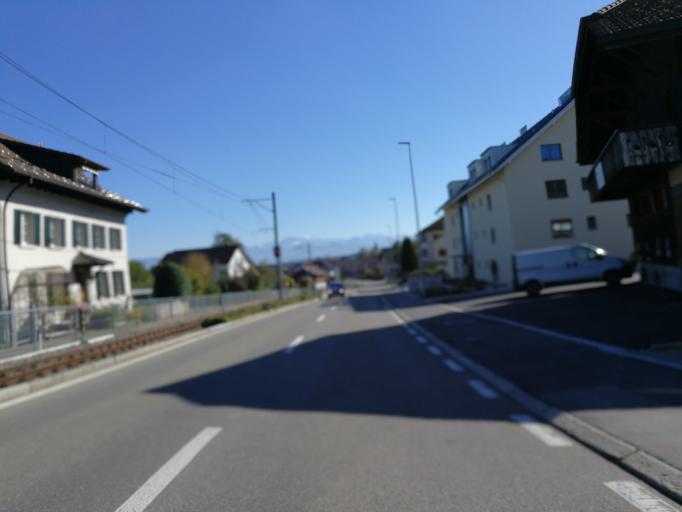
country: CH
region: Zurich
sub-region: Bezirk Uster
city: Hinteregg
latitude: 47.3081
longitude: 8.6820
